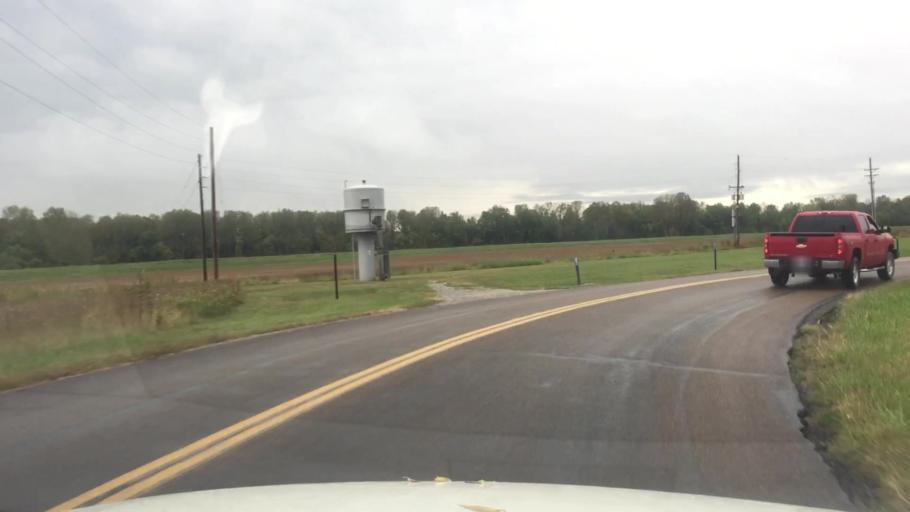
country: US
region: Missouri
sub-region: Boone County
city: Columbia
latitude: 38.8871
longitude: -92.4668
